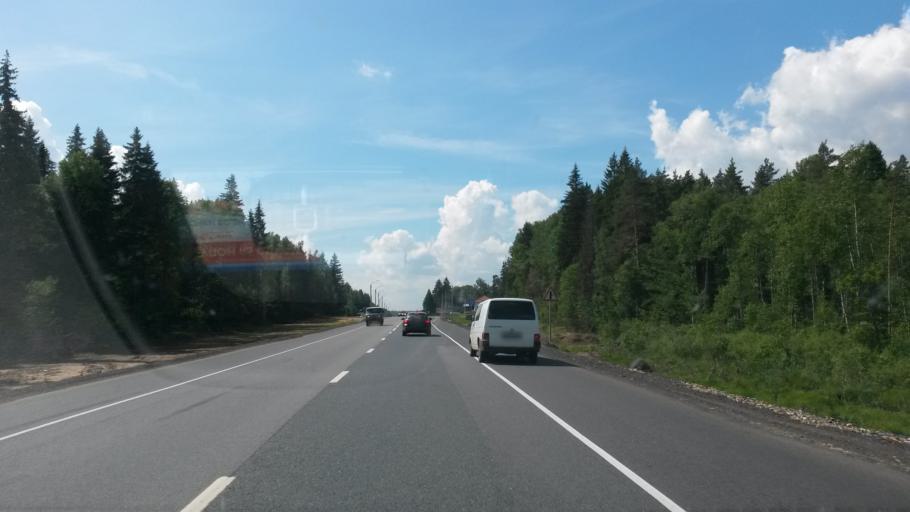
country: RU
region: Jaroslavl
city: Pereslavl'-Zalesskiy
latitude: 56.8448
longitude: 38.9285
